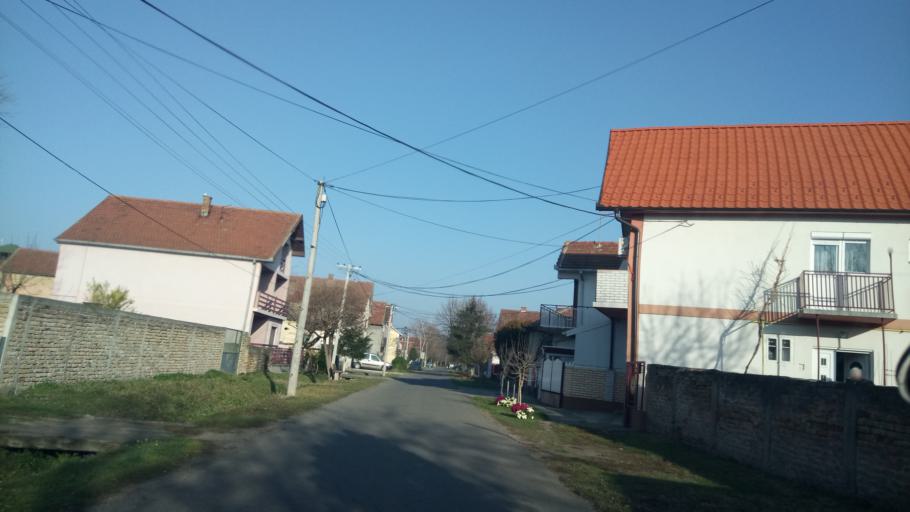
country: RS
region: Autonomna Pokrajina Vojvodina
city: Nova Pazova
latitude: 44.9370
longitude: 20.2127
